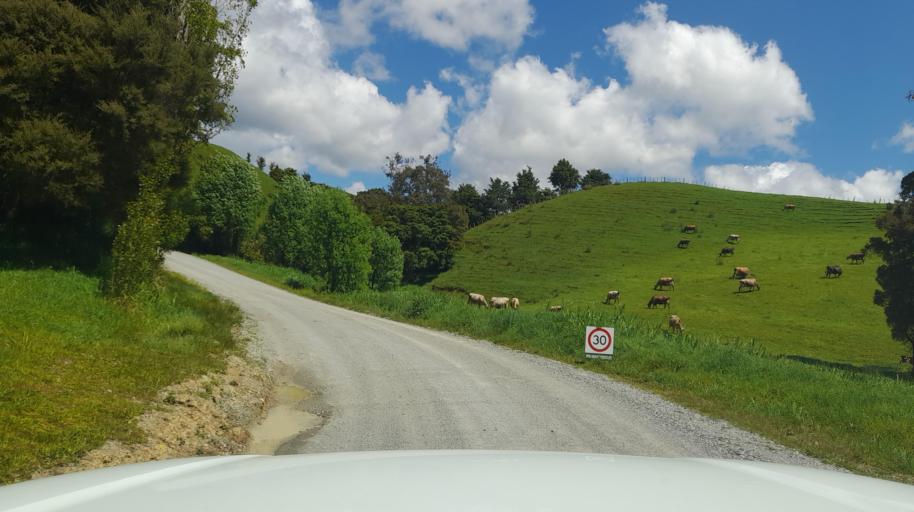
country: NZ
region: Northland
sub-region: Far North District
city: Taipa
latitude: -35.1216
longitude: 173.4066
